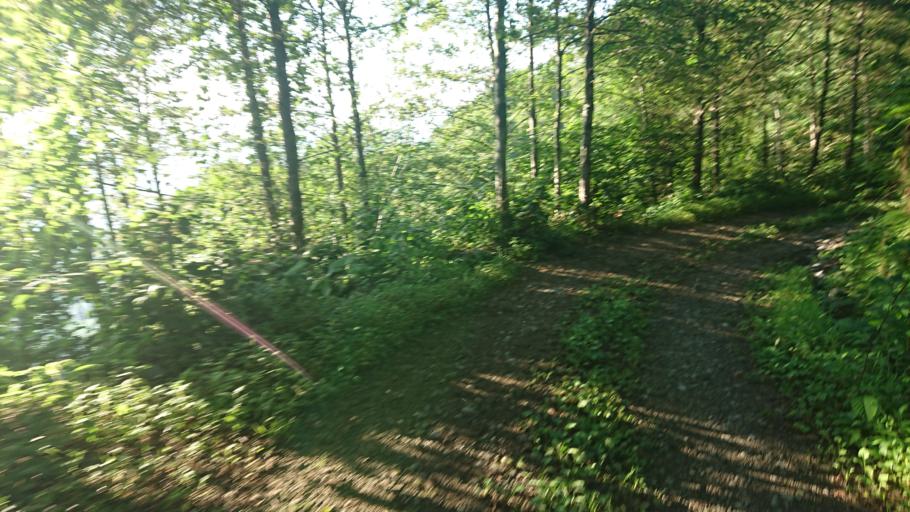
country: TR
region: Rize
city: Rize
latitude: 40.9773
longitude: 40.4984
